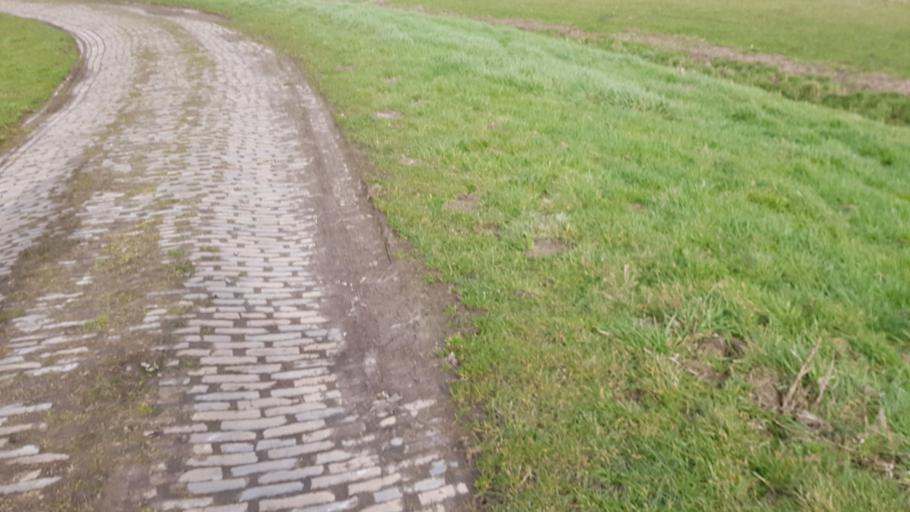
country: NL
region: Utrecht
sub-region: Gemeente Baarn
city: Baarn
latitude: 52.2575
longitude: 5.2988
